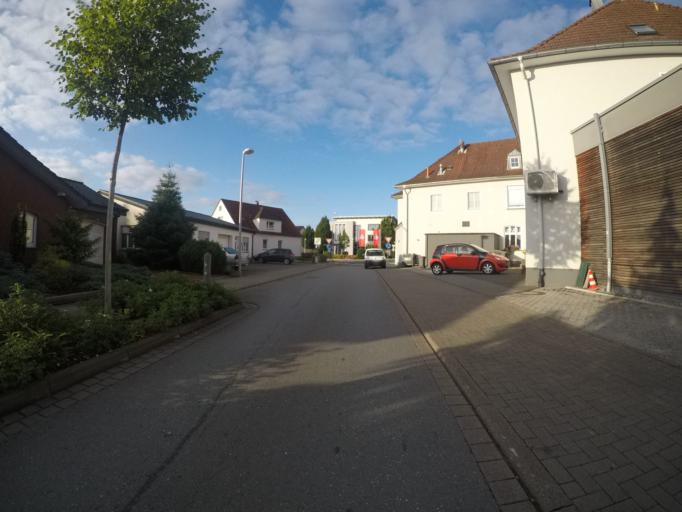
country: DE
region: North Rhine-Westphalia
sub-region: Regierungsbezirk Detmold
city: Hiddenhausen
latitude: 52.1280
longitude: 8.6276
